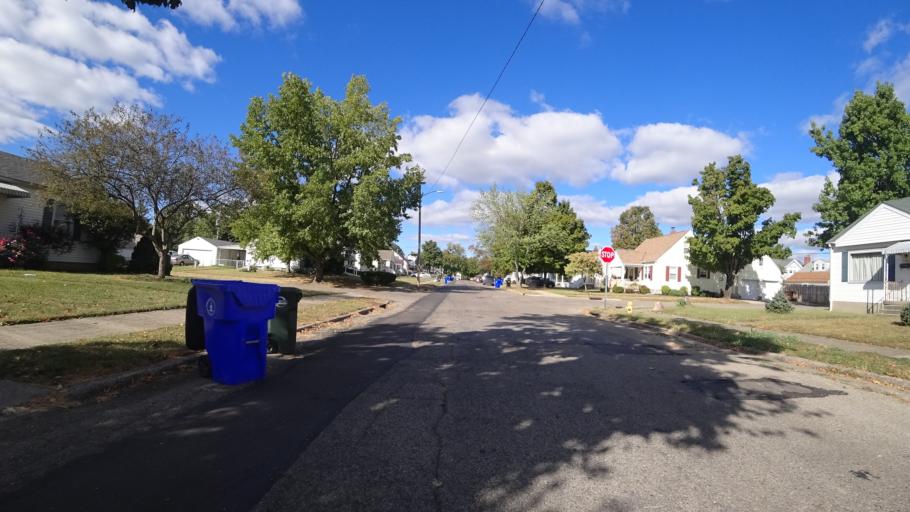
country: US
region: Ohio
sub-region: Butler County
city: Fairfield
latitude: 39.3643
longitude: -84.5494
